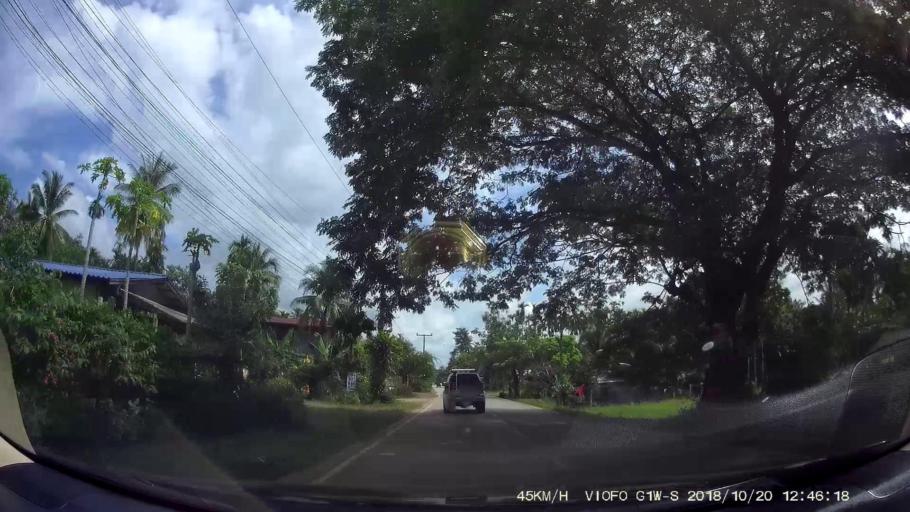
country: TH
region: Chaiyaphum
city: Khon San
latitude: 16.5339
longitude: 101.8794
